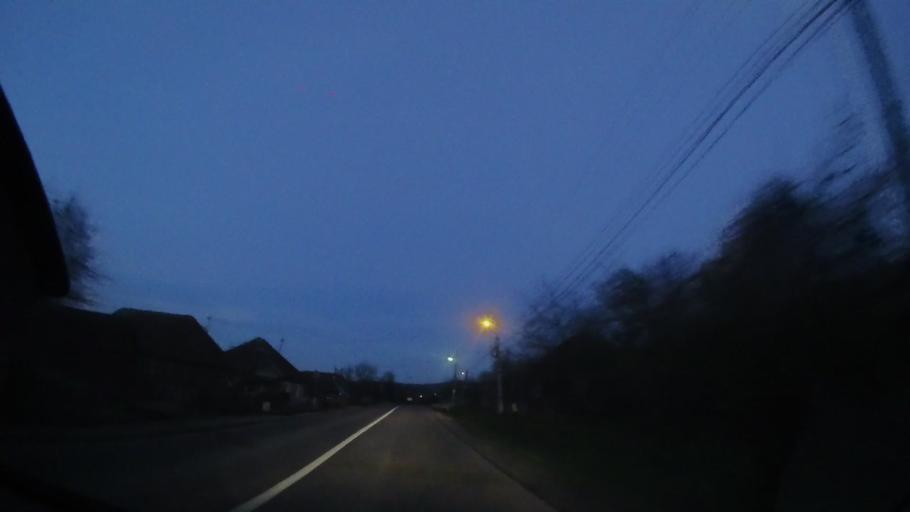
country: RO
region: Mures
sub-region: Comuna Sarmasu
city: Sarmasu
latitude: 46.7629
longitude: 24.1810
